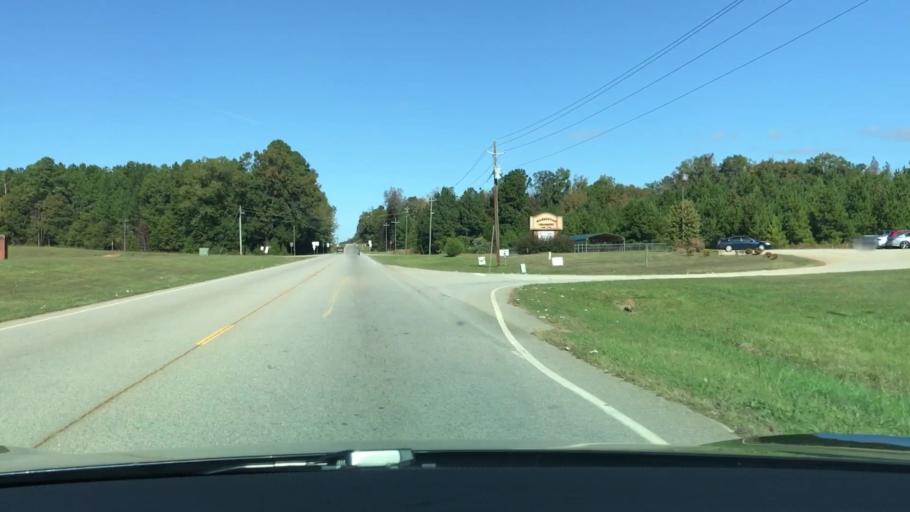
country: US
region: Georgia
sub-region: Warren County
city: West Warrenton
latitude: 33.4180
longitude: -82.6785
